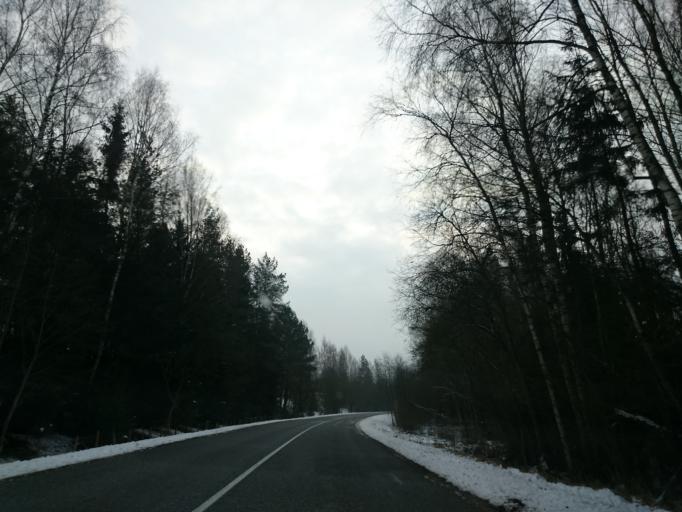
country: LV
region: Seja
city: Loja
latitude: 57.1819
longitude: 24.6053
